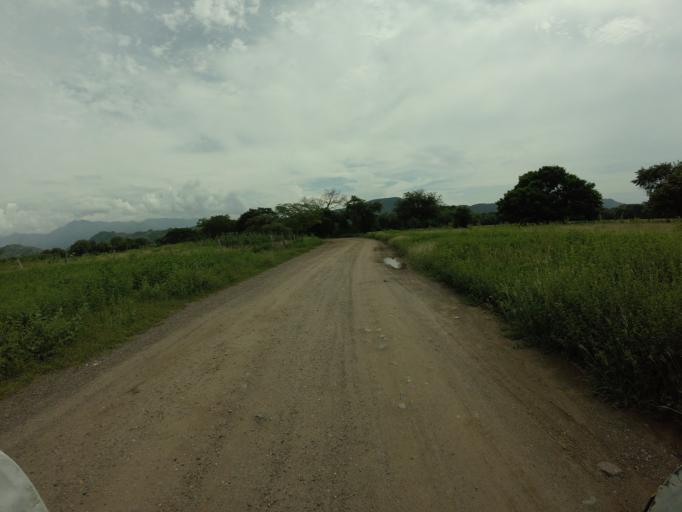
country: CO
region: Tolima
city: Natagaima
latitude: 3.4459
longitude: -75.1407
